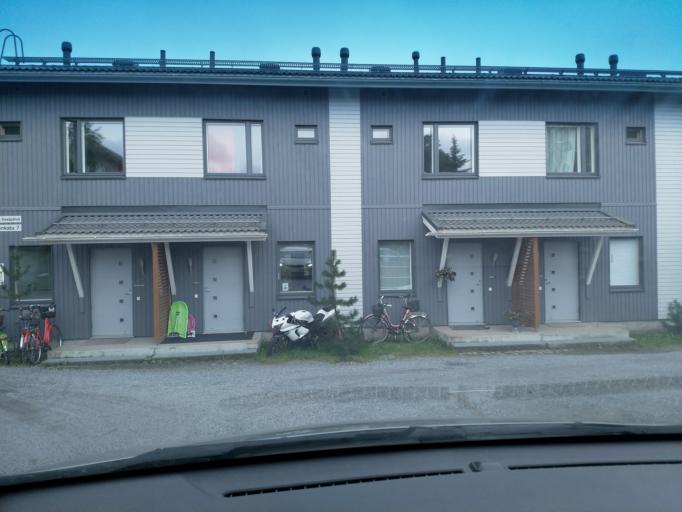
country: FI
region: Pirkanmaa
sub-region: Tampere
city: Tampere
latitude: 61.4753
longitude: 23.8324
